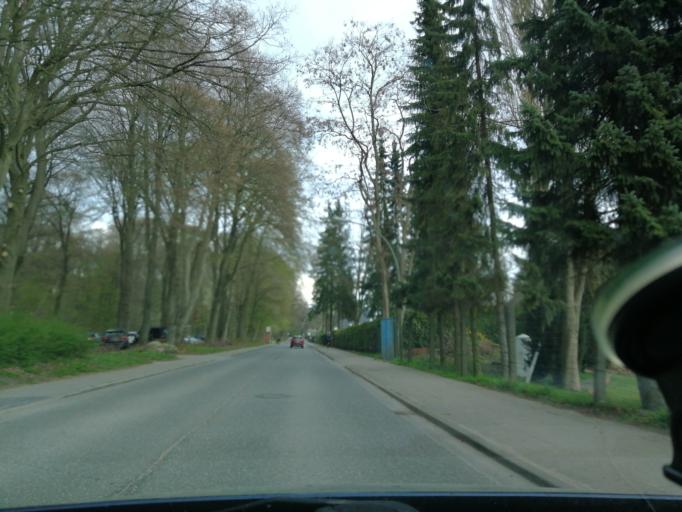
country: DE
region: Hamburg
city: Harburg
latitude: 53.4570
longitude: 9.9355
